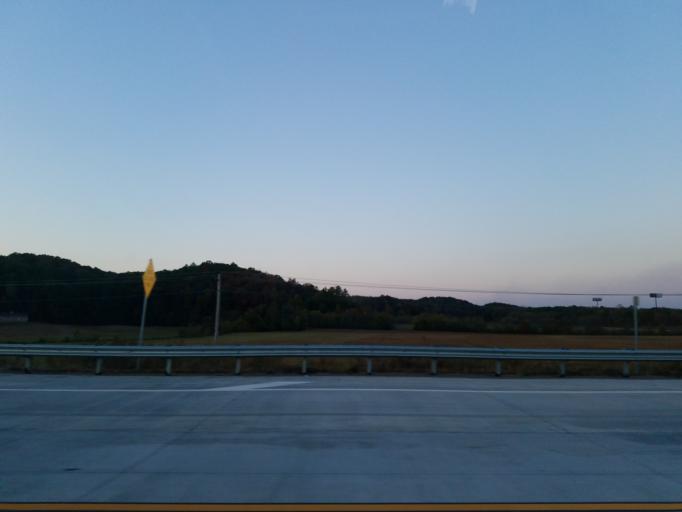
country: US
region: Georgia
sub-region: Gordon County
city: Calhoun
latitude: 34.5762
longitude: -84.9547
